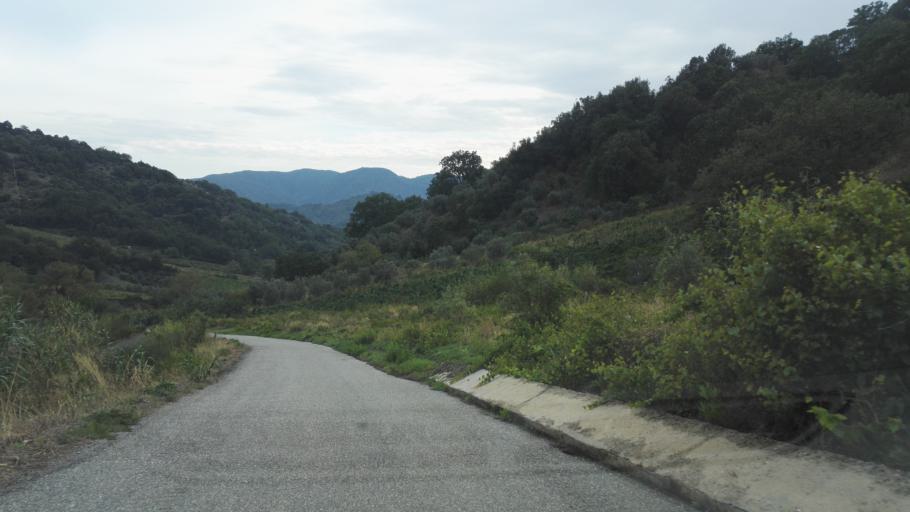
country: IT
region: Calabria
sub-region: Provincia di Reggio Calabria
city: Caulonia
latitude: 38.4316
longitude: 16.3941
